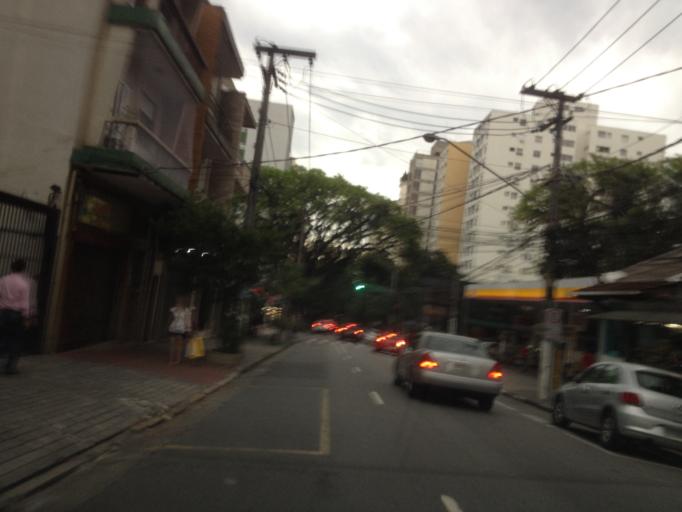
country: BR
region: Sao Paulo
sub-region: Sao Paulo
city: Sao Paulo
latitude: -23.5608
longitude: -46.6684
